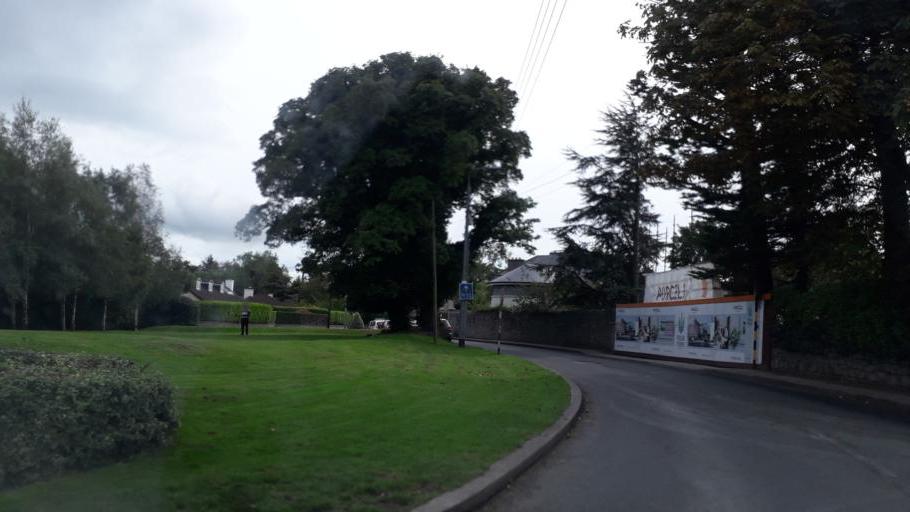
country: IE
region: Leinster
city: Foxrock
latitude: 53.2592
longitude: -6.1710
